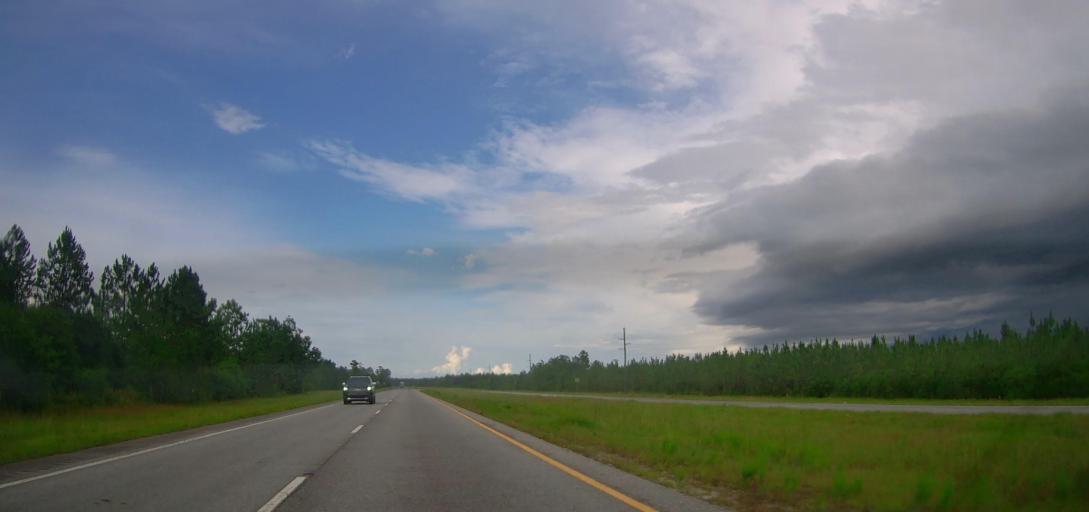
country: US
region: Georgia
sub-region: Pierce County
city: Blackshear
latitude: 31.4433
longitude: -82.0742
